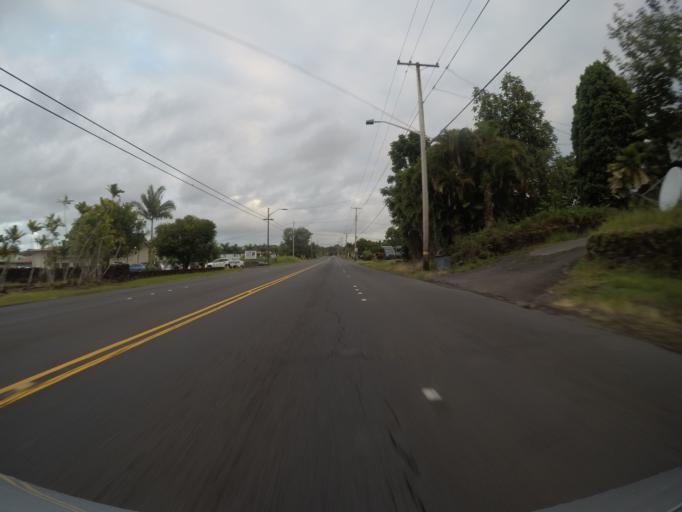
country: US
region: Hawaii
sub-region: Hawaii County
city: Hilo
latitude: 19.6793
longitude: -155.0671
